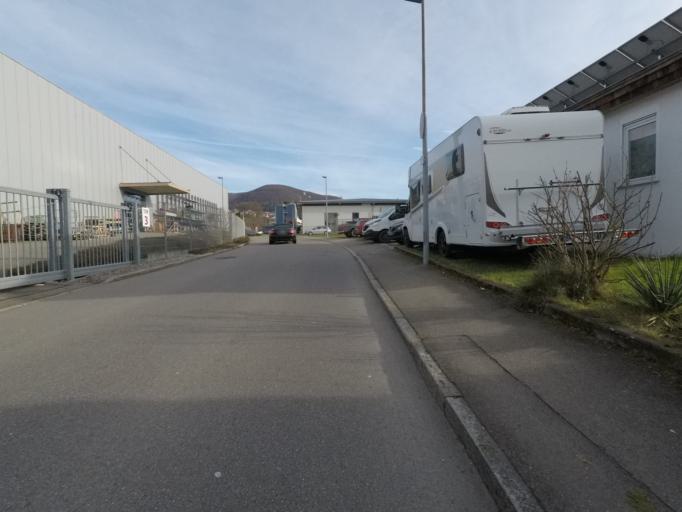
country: DE
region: Baden-Wuerttemberg
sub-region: Tuebingen Region
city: Eningen unter Achalm
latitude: 48.4771
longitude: 9.2479
